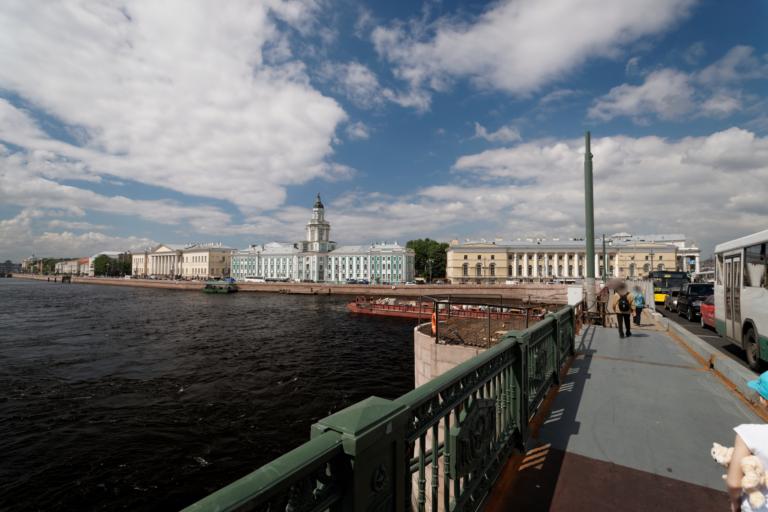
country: RU
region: St.-Petersburg
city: Saint Petersburg
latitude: 59.9410
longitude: 30.3082
